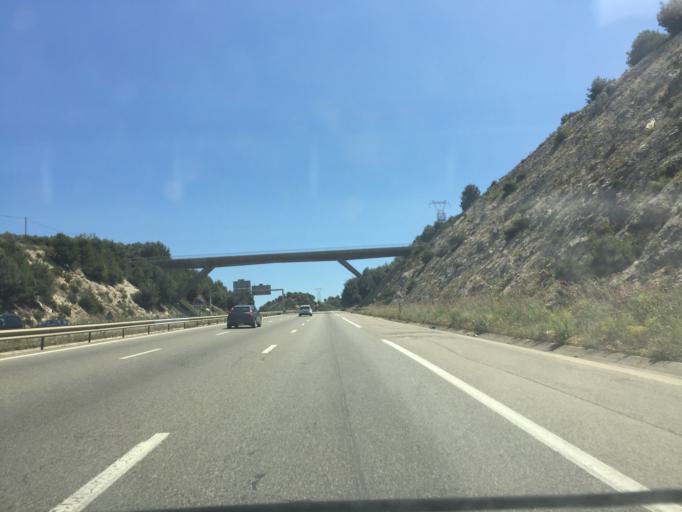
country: FR
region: Provence-Alpes-Cote d'Azur
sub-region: Departement des Bouches-du-Rhone
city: Les Pennes-Mirabeau
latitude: 43.3901
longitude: 5.3028
